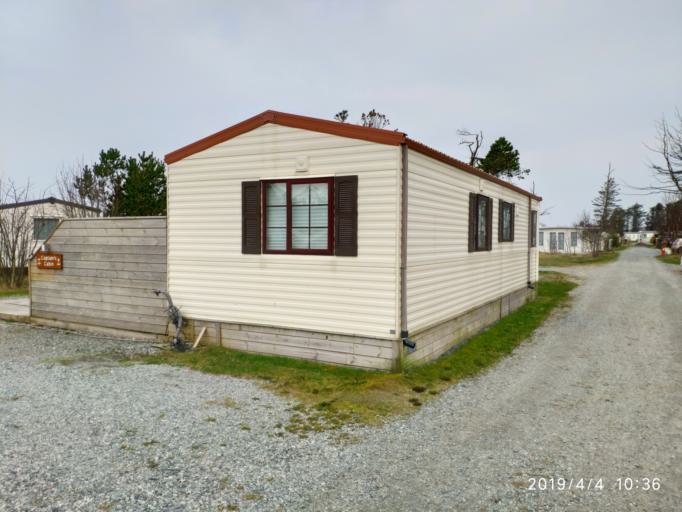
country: NO
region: Rogaland
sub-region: Klepp
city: Kleppe
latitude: 58.8004
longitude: 5.5584
